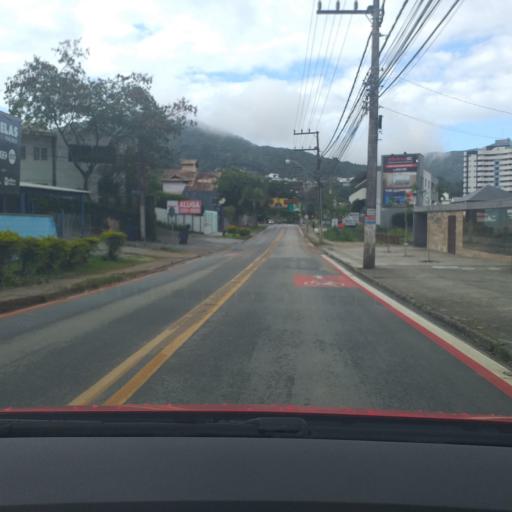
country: BR
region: Santa Catarina
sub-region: Florianopolis
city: Corrego Grande
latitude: -27.5984
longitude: -48.4988
